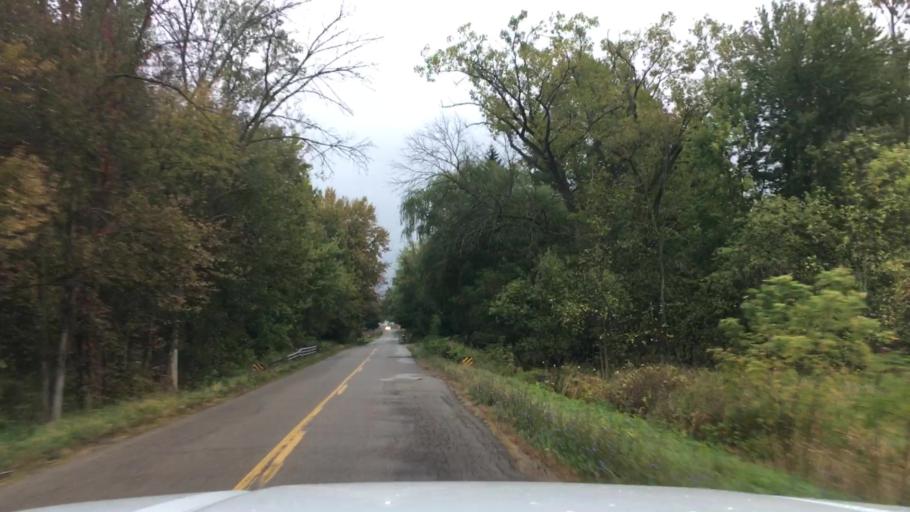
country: US
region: Michigan
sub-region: Ottawa County
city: Hudsonville
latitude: 42.8407
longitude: -85.8115
